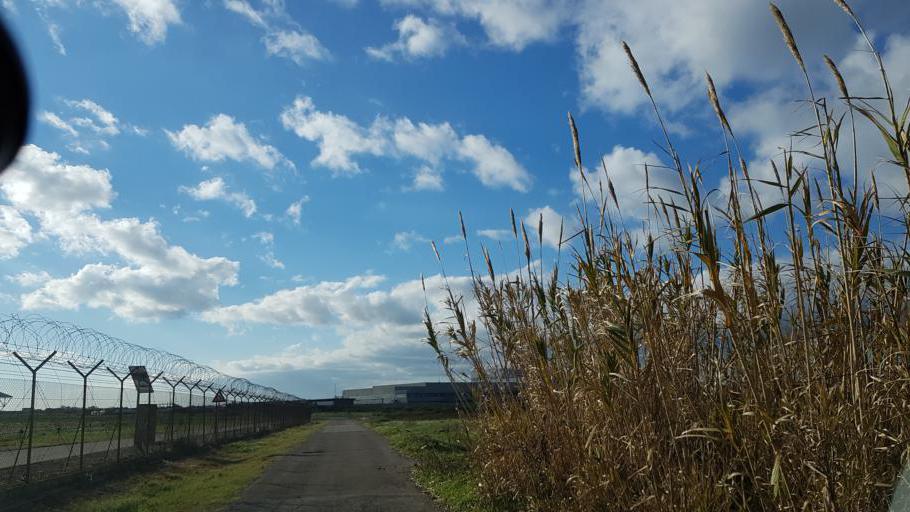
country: IT
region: Apulia
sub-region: Provincia di Brindisi
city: Materdomini
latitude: 40.6771
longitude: 17.9224
